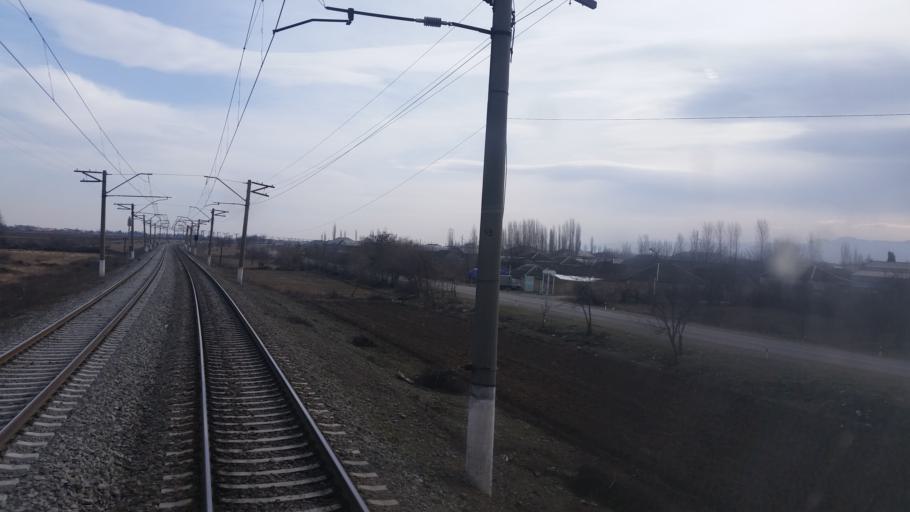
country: AZ
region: Shamkir Rayon
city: Dzagam
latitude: 40.9398
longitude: 45.7608
